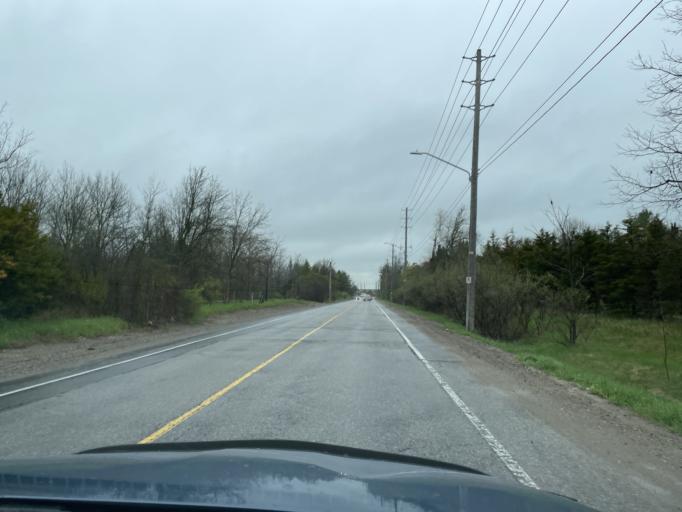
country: CA
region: Ontario
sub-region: Wellington County
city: Guelph
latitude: 43.5423
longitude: -80.2187
